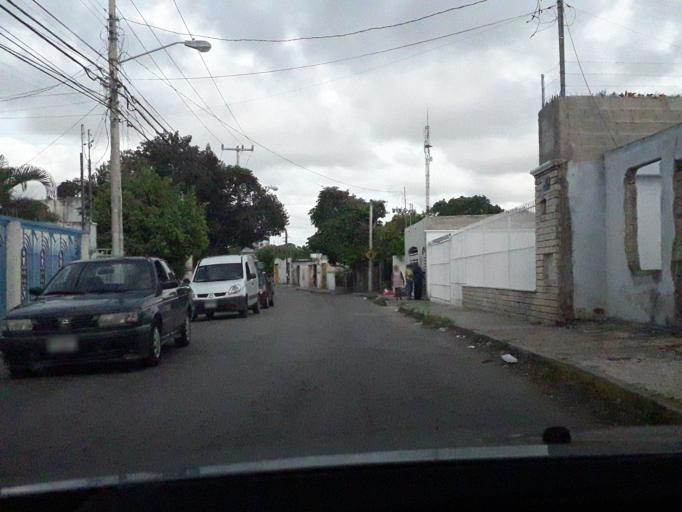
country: MX
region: Yucatan
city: Merida
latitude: 21.0204
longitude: -89.6373
